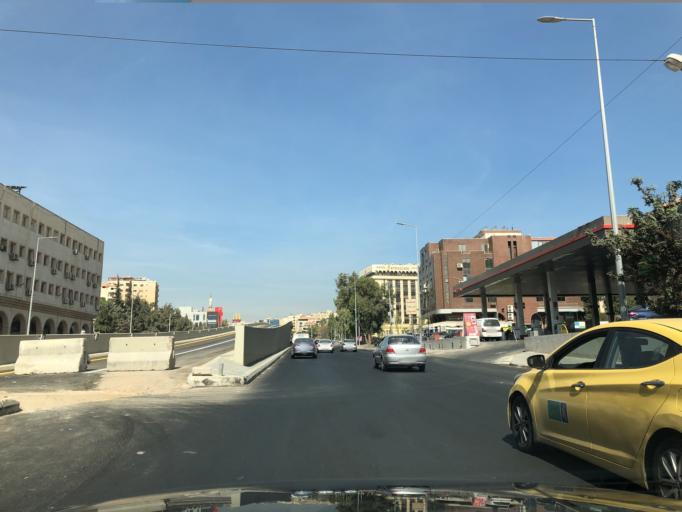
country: JO
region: Amman
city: Al Jubayhah
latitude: 31.9896
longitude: 35.8939
